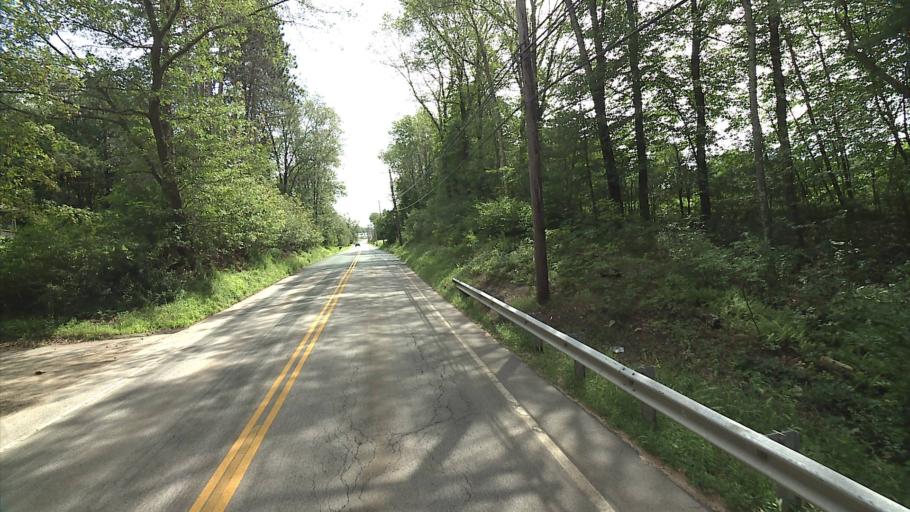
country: US
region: Connecticut
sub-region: Windham County
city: South Woodstock
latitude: 41.9389
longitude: -71.9965
